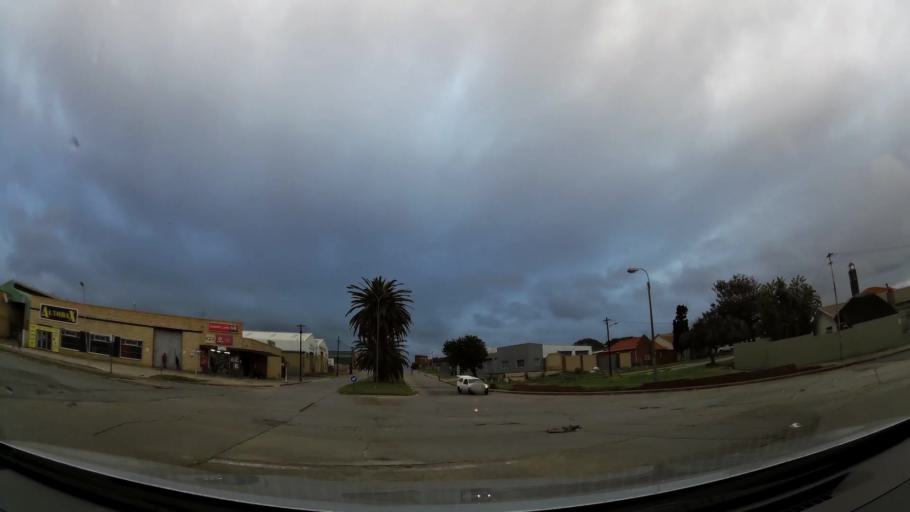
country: ZA
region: Eastern Cape
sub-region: Nelson Mandela Bay Metropolitan Municipality
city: Port Elizabeth
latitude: -33.9191
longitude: 25.5928
